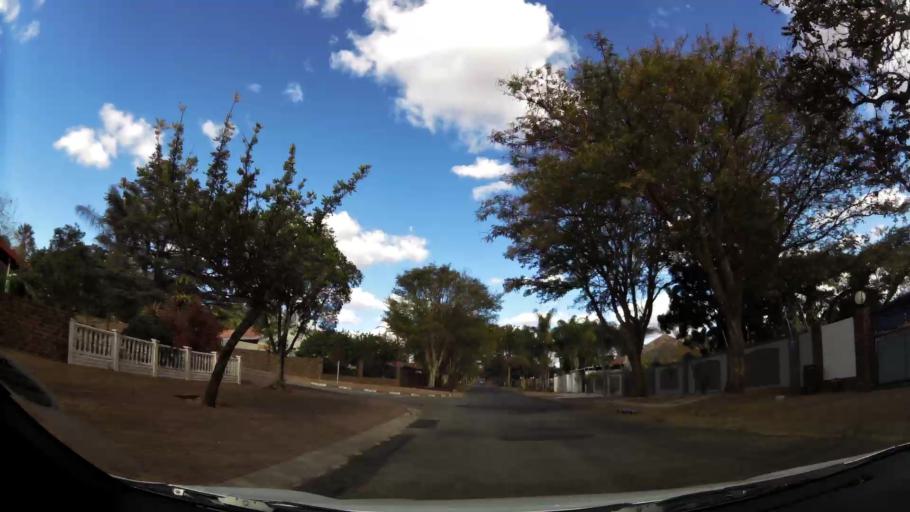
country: ZA
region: Limpopo
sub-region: Capricorn District Municipality
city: Polokwane
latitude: -23.8920
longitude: 29.4809
